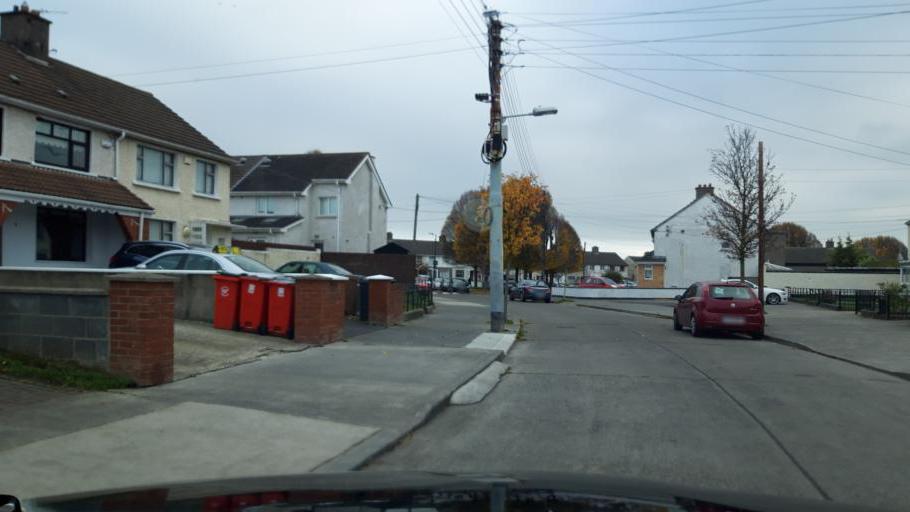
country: IE
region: Leinster
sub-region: Dublin City
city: Finglas
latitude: 53.3834
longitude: -6.2813
